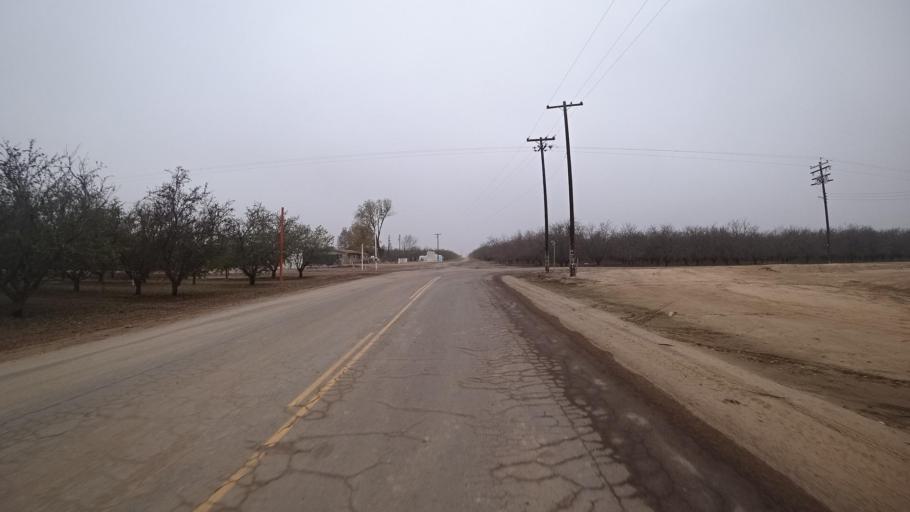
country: US
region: California
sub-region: Kern County
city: Wasco
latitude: 35.5575
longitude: -119.4915
